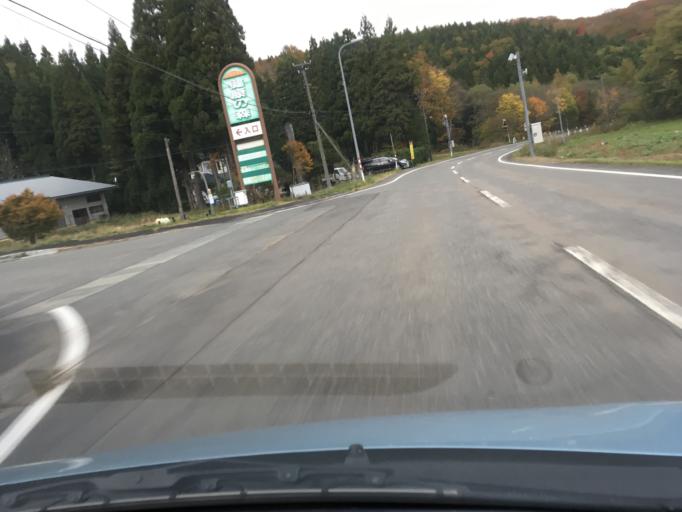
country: JP
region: Iwate
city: Ichinoseki
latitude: 39.0114
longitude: 140.8659
